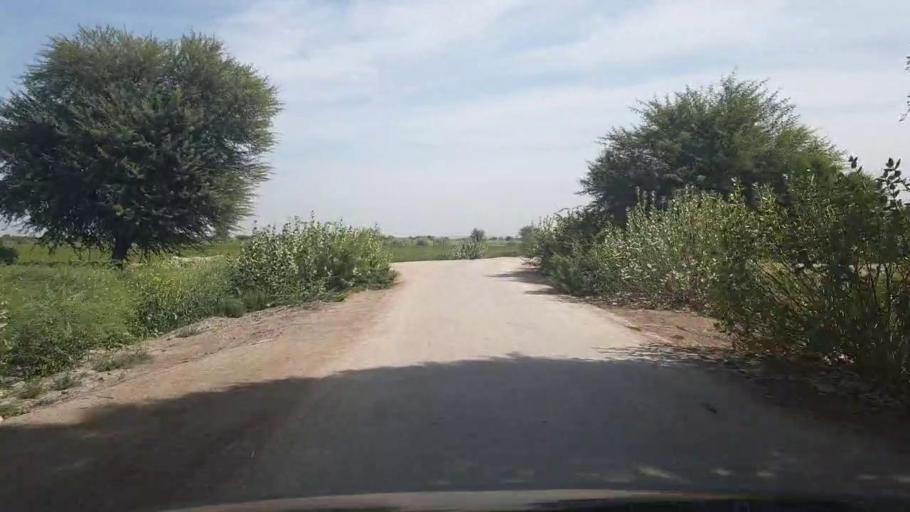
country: PK
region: Sindh
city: Kunri
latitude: 25.2143
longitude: 69.6378
